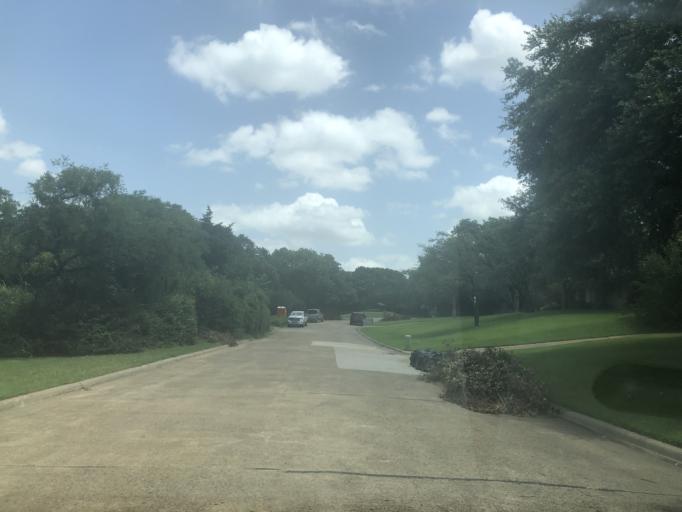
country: US
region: Texas
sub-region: Dallas County
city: University Park
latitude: 32.8805
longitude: -96.8231
